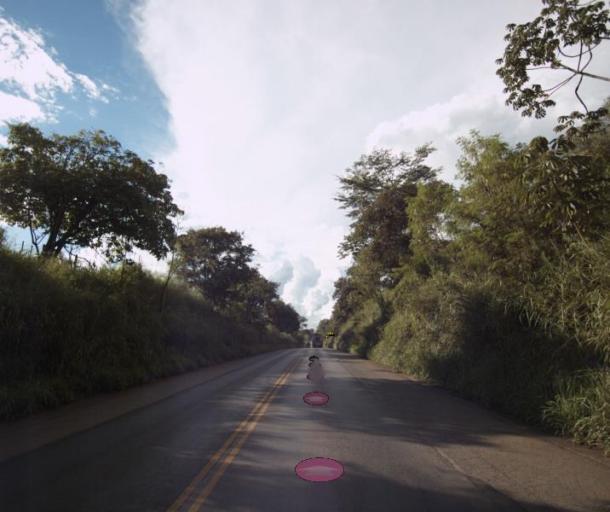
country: BR
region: Goias
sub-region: Rialma
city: Rialma
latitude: -15.3261
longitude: -49.5712
